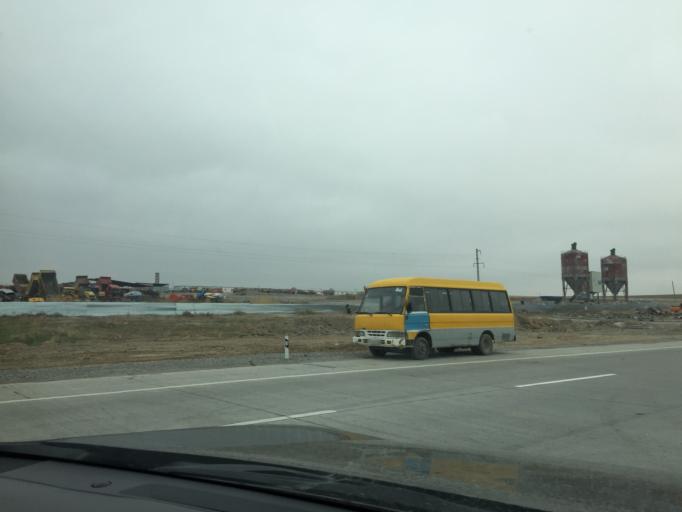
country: KZ
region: Ongtustik Qazaqstan
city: Aksu
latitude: 42.4800
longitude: 69.8577
